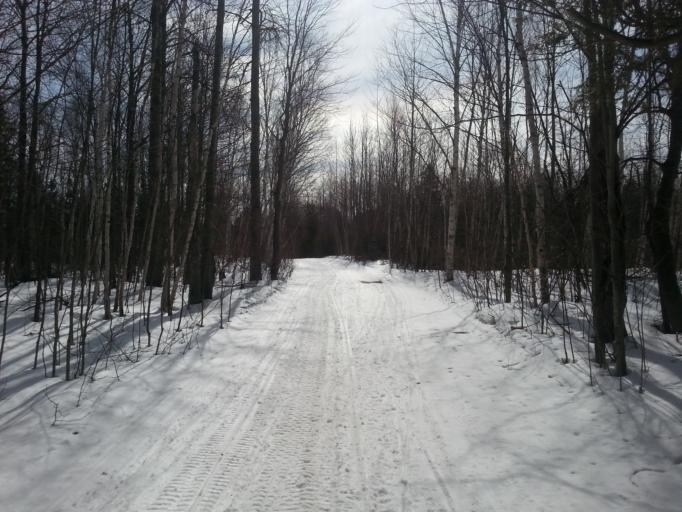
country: CA
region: Ontario
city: Greater Sudbury
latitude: 46.3455
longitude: -80.9014
